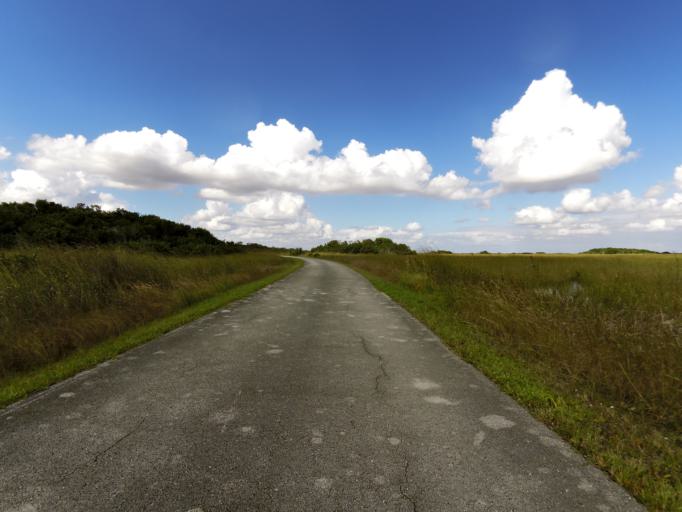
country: US
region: Florida
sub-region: Miami-Dade County
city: The Hammocks
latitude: 25.6712
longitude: -80.7596
